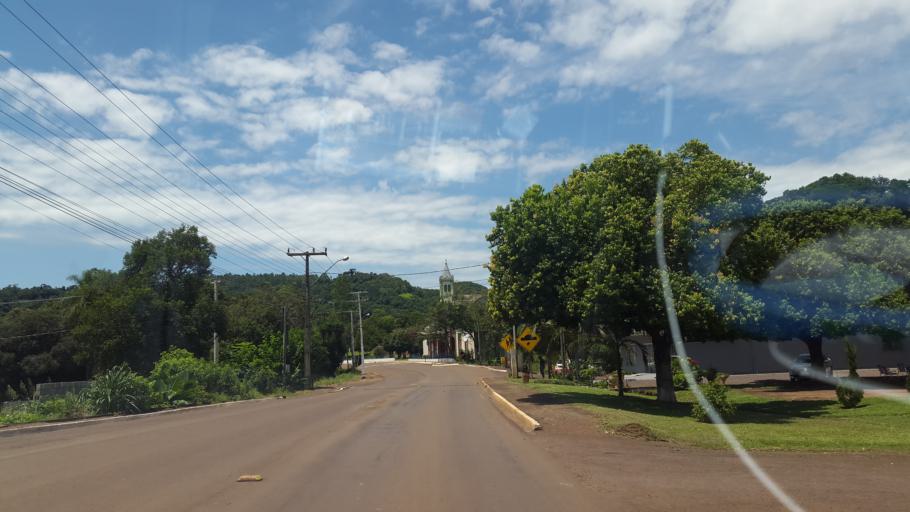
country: BR
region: Rio Grande do Sul
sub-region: Frederico Westphalen
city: Frederico Westphalen
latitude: -27.0680
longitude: -53.4290
